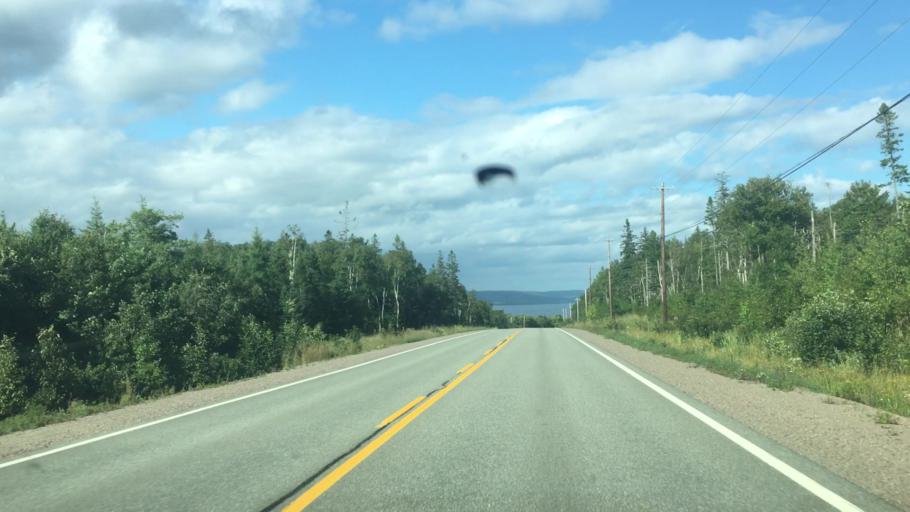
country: CA
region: Nova Scotia
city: Sydney
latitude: 45.8597
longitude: -60.6274
